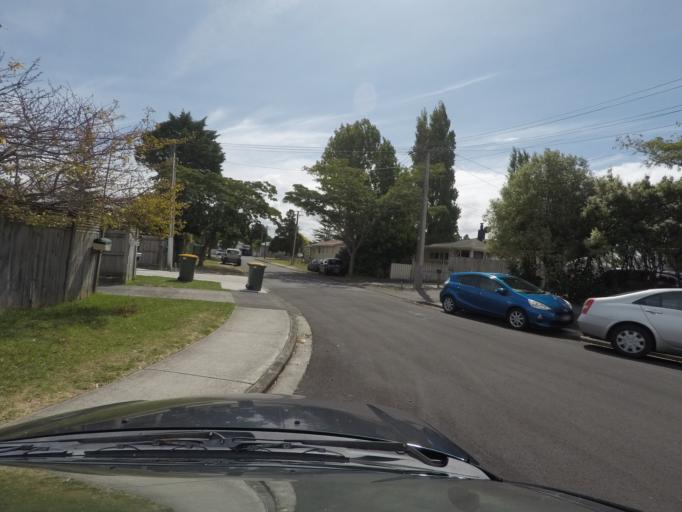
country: NZ
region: Auckland
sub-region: Auckland
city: Rosebank
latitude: -36.8919
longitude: 174.6688
